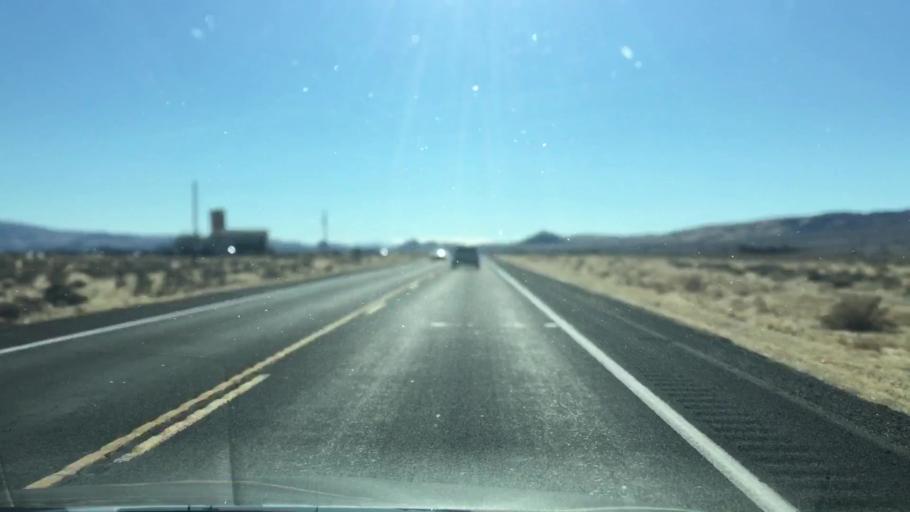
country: US
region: Nevada
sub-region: Lyon County
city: Silver Springs
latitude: 39.3896
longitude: -119.2306
